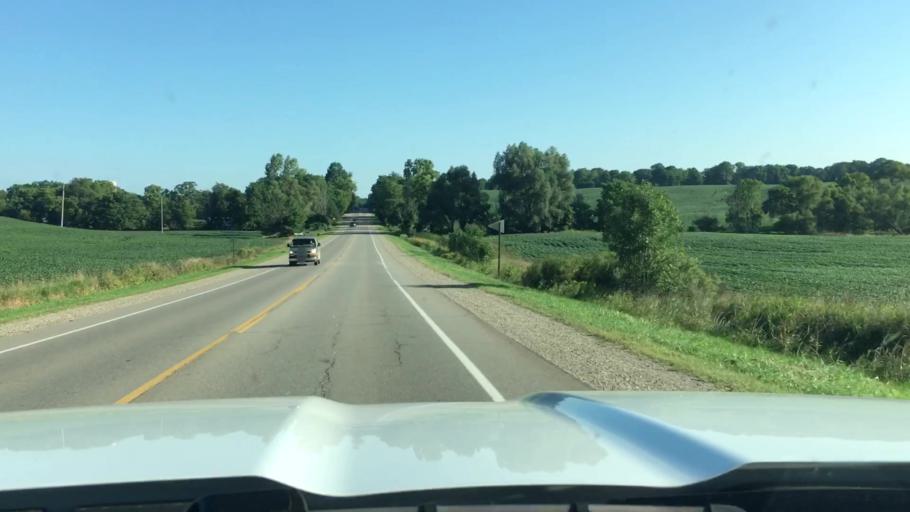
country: US
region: Michigan
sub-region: Kent County
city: Lowell
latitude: 42.8884
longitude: -85.3710
